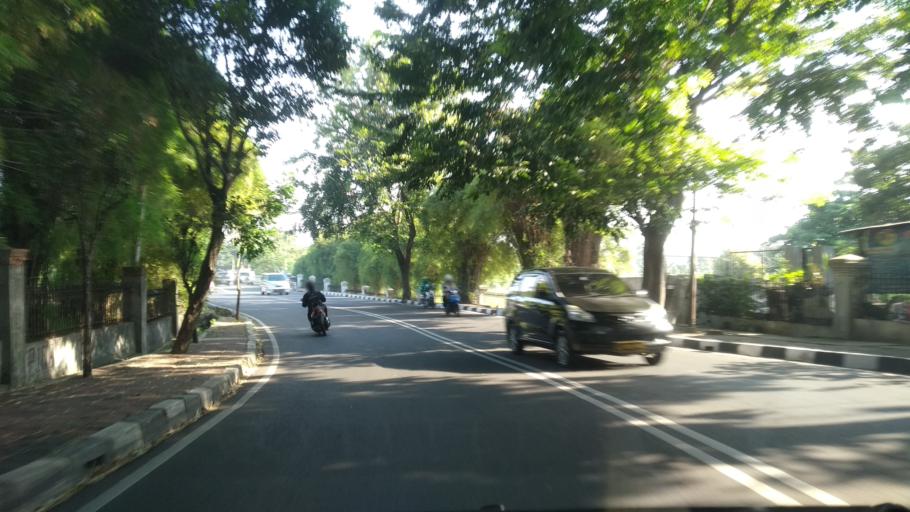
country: ID
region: Banten
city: South Tangerang
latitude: -6.2536
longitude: 106.7694
